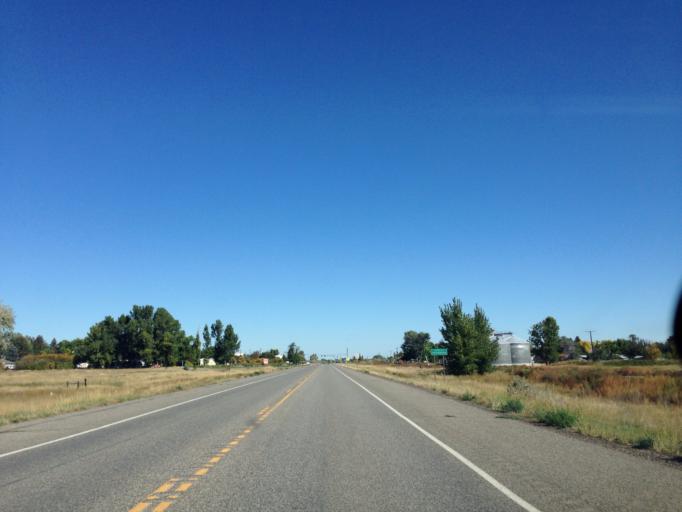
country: US
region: Montana
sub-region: Yellowstone County
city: Laurel
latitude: 45.3873
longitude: -108.9096
